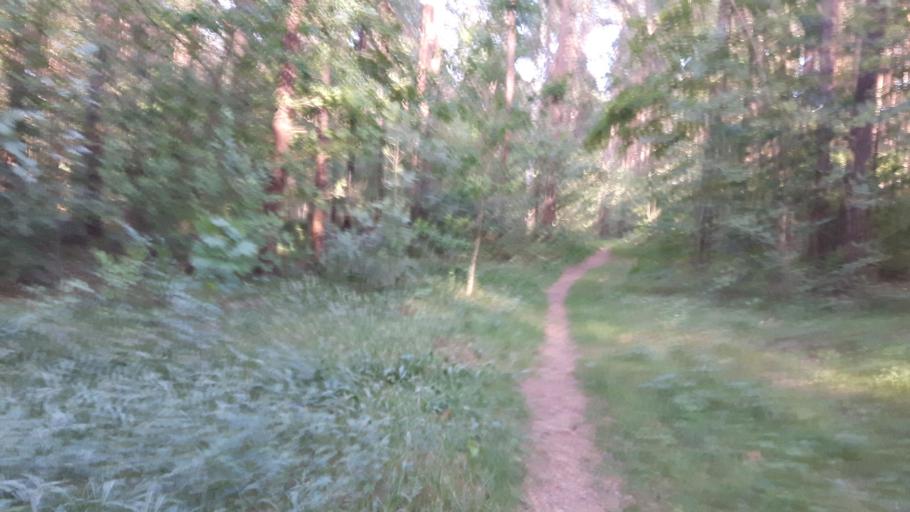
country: LV
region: Riga
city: Jaunciems
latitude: 57.0106
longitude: 24.1368
